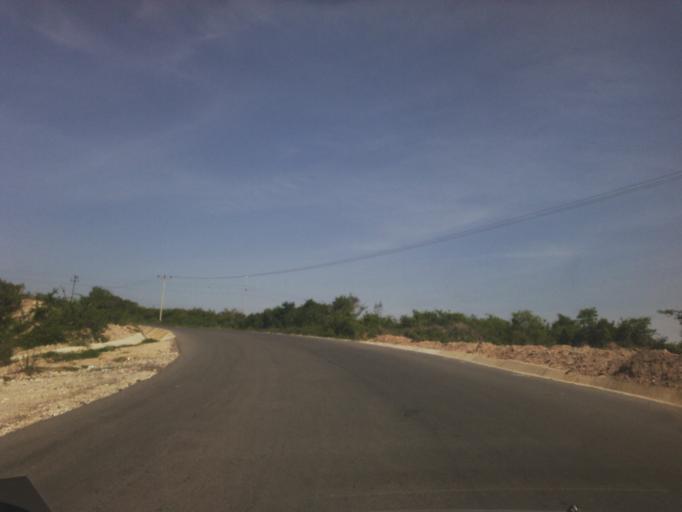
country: TZ
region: Dar es Salaam
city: Magomeni
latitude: -6.7794
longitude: 39.1974
